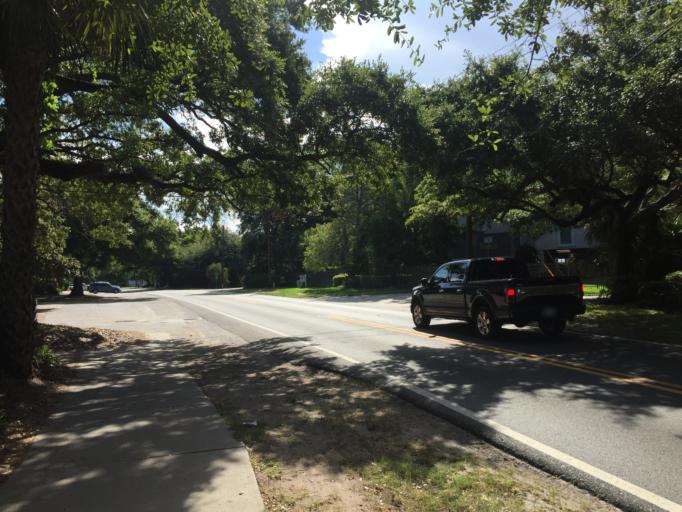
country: US
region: Georgia
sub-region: Glynn County
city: Saint Simons Island
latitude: 31.1356
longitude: -81.3880
